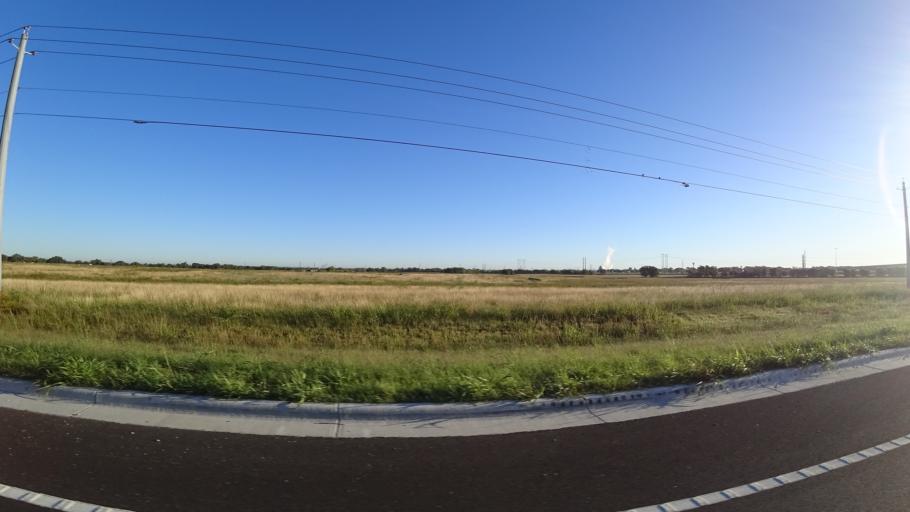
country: US
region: Texas
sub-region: Travis County
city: Hornsby Bend
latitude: 30.1994
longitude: -97.6301
